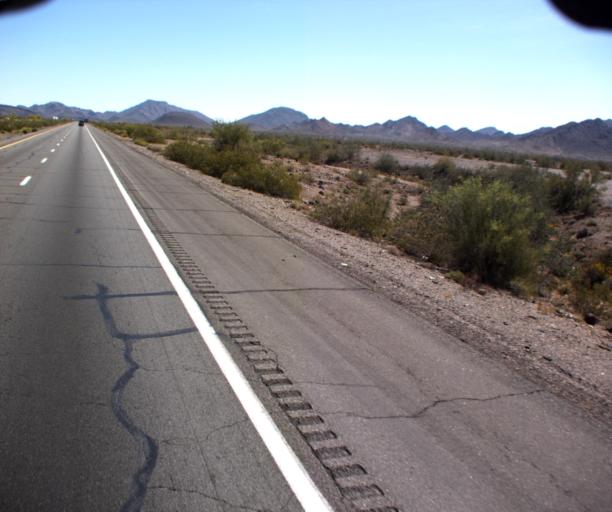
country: US
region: Arizona
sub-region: La Paz County
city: Quartzsite
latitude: 33.6744
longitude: -114.1341
